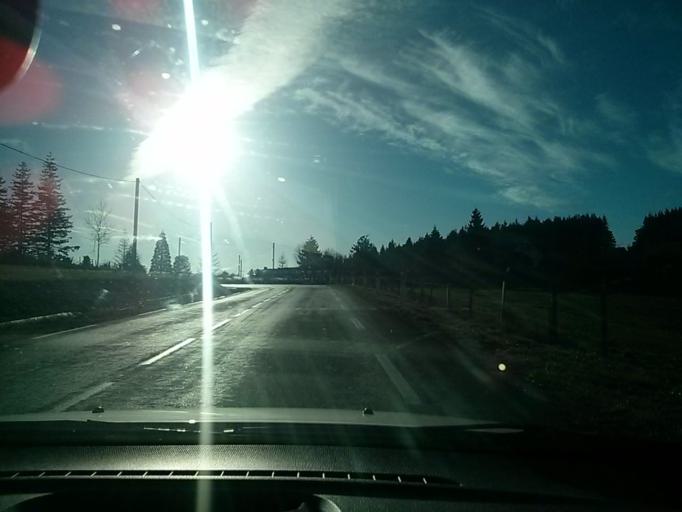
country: FR
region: Rhone-Alpes
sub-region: Departement de la Loire
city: Saint-Genest-Malifaux
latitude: 45.3743
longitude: 4.4957
